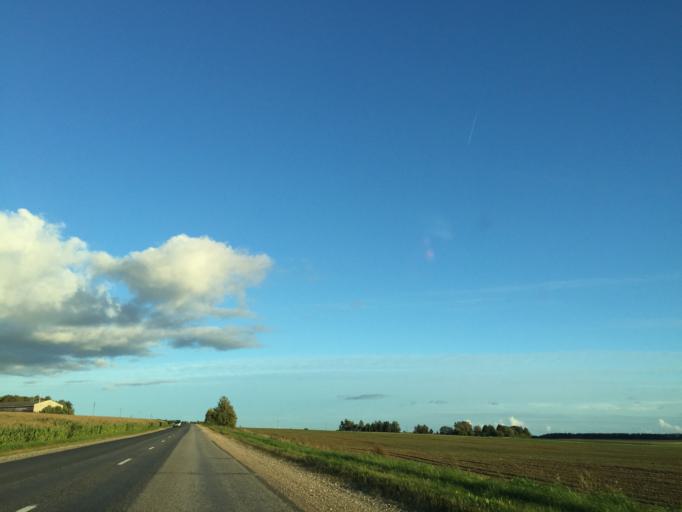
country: LV
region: Saldus Rajons
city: Saldus
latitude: 56.7090
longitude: 22.4182
